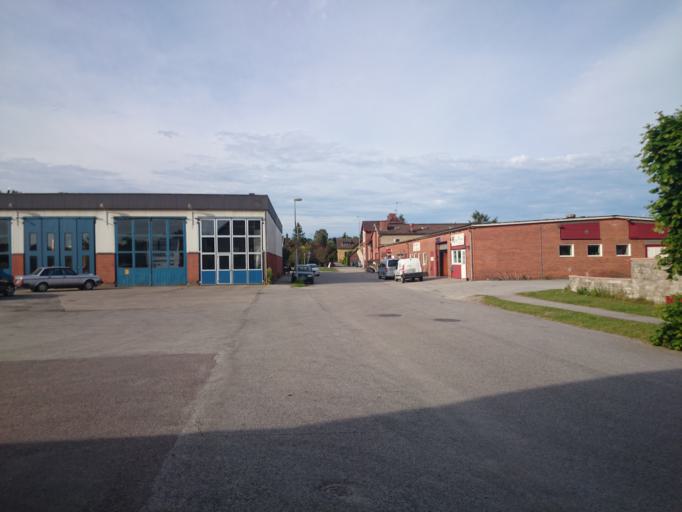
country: SE
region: Skane
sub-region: Lunds Kommun
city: Genarp
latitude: 55.7179
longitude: 13.3467
